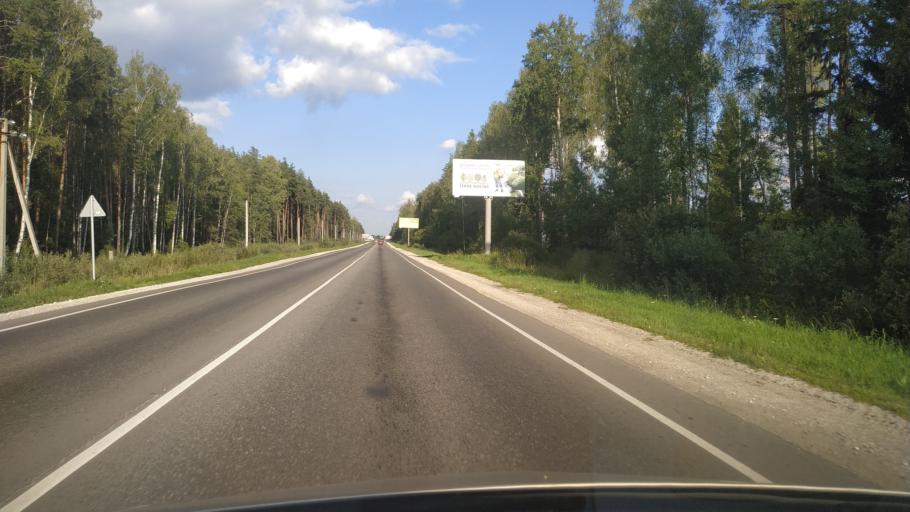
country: RU
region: Moskovskaya
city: Shaturtorf
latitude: 55.5784
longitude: 39.4425
